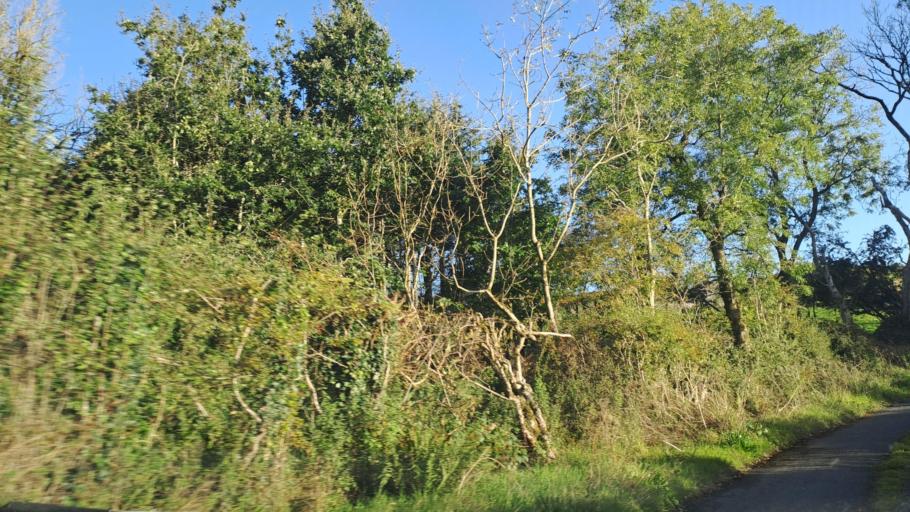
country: IE
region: Ulster
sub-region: An Cabhan
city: Kingscourt
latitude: 53.9813
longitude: -6.8497
